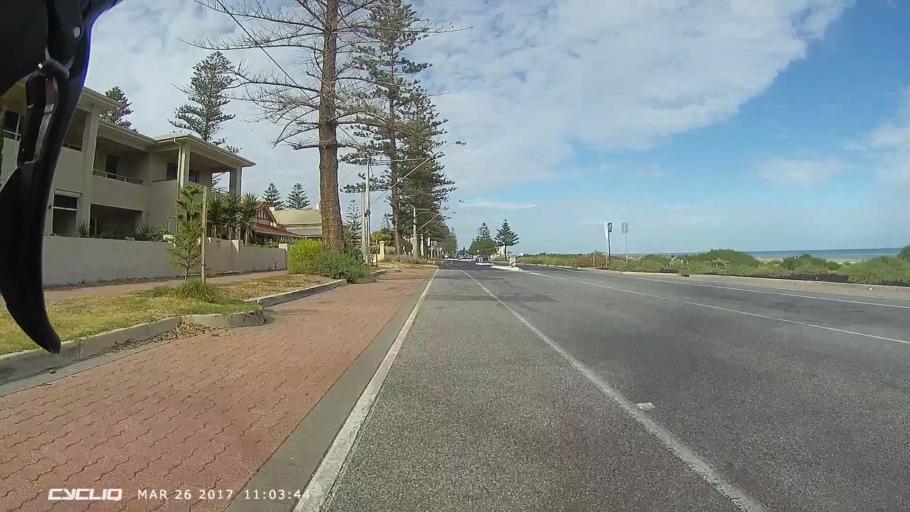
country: AU
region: South Australia
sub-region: Port Adelaide Enfield
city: Birkenhead
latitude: -34.8318
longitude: 138.4830
